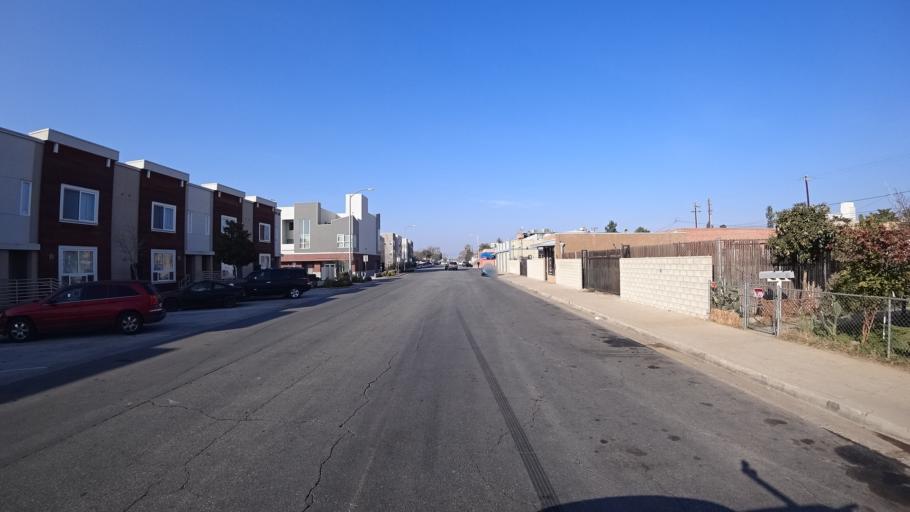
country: US
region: California
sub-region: Kern County
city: Bakersfield
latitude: 35.3797
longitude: -118.9908
